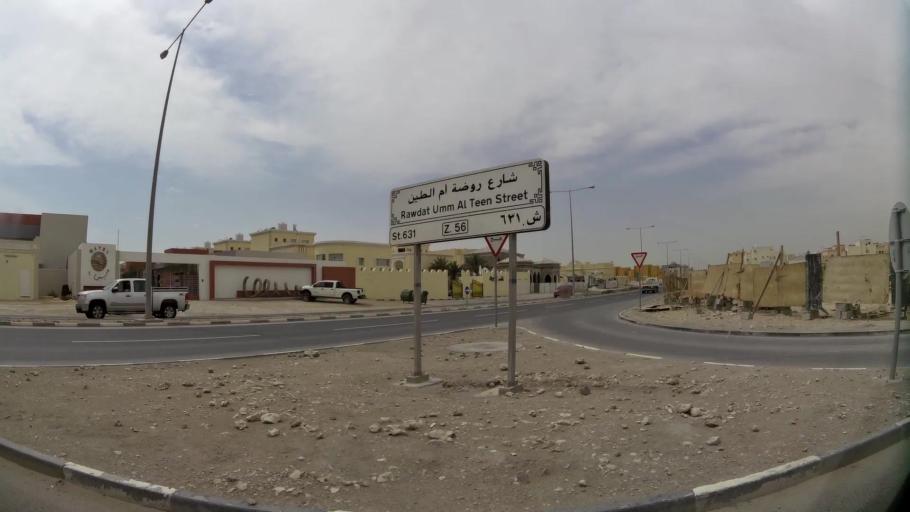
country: QA
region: Baladiyat ad Dawhah
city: Doha
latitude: 25.2177
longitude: 51.4757
